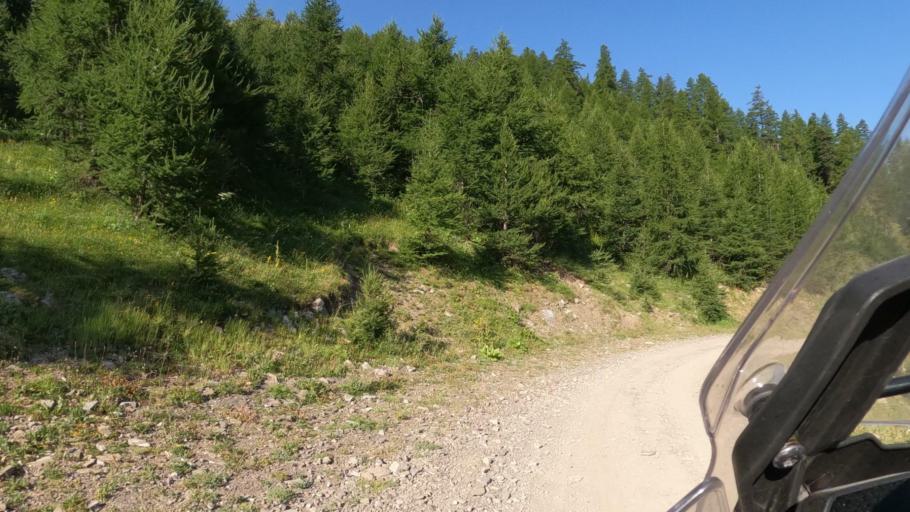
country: FR
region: Provence-Alpes-Cote d'Azur
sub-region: Departement des Hautes-Alpes
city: Guillestre
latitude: 44.5858
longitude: 6.6209
